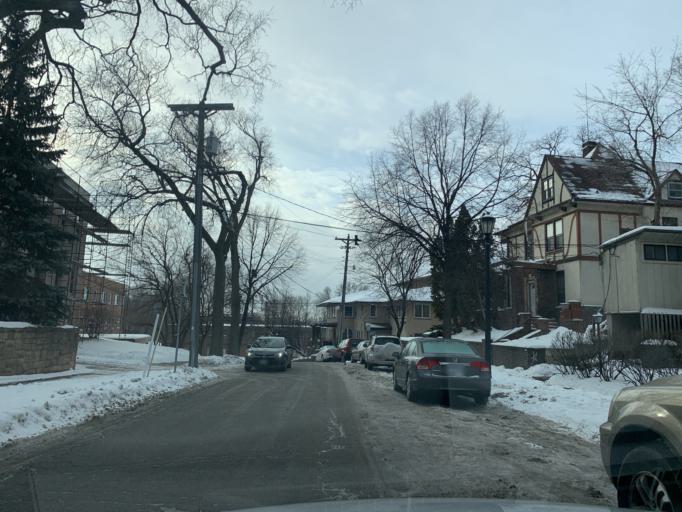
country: US
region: Minnesota
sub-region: Hennepin County
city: Minneapolis
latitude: 44.9636
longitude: -93.2833
